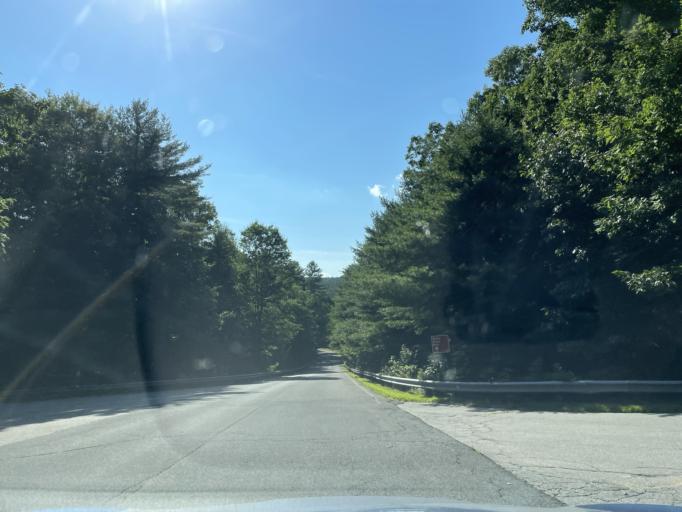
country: US
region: Massachusetts
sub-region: Worcester County
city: Sturbridge
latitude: 42.1465
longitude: -72.0552
